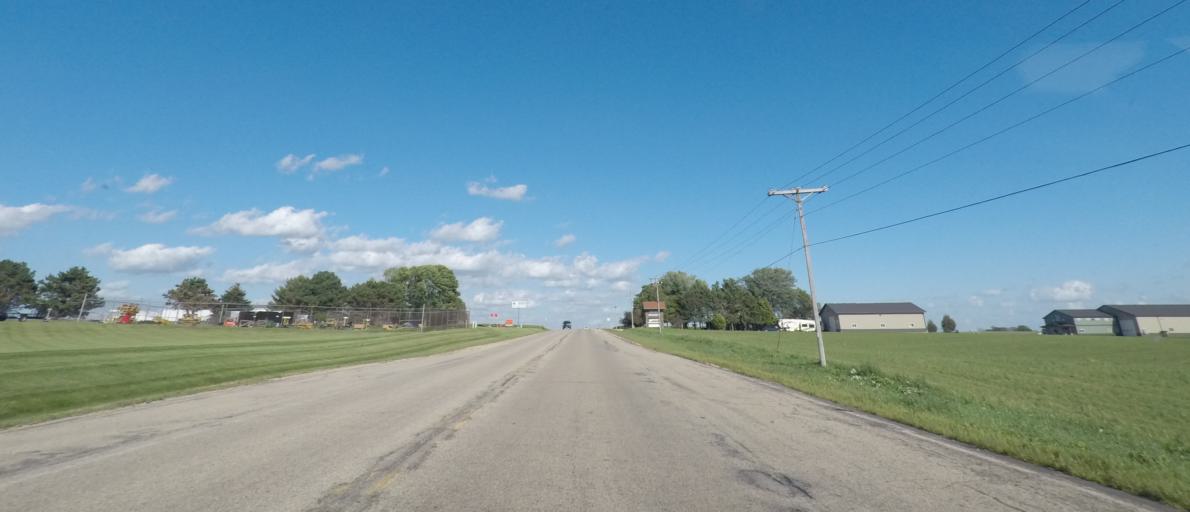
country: US
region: Wisconsin
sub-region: Iowa County
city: Dodgeville
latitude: 42.9817
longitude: -90.1059
